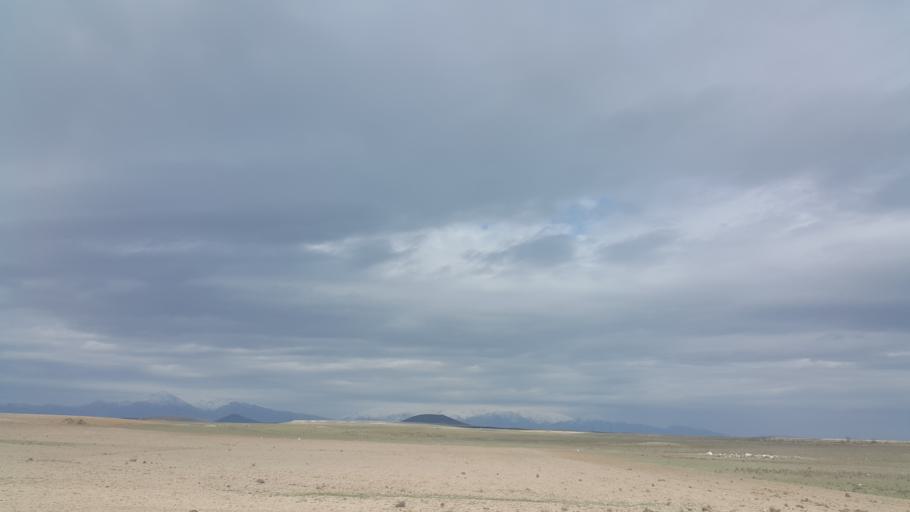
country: TR
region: Nigde
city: Altunhisar
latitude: 37.8811
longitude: 34.1485
